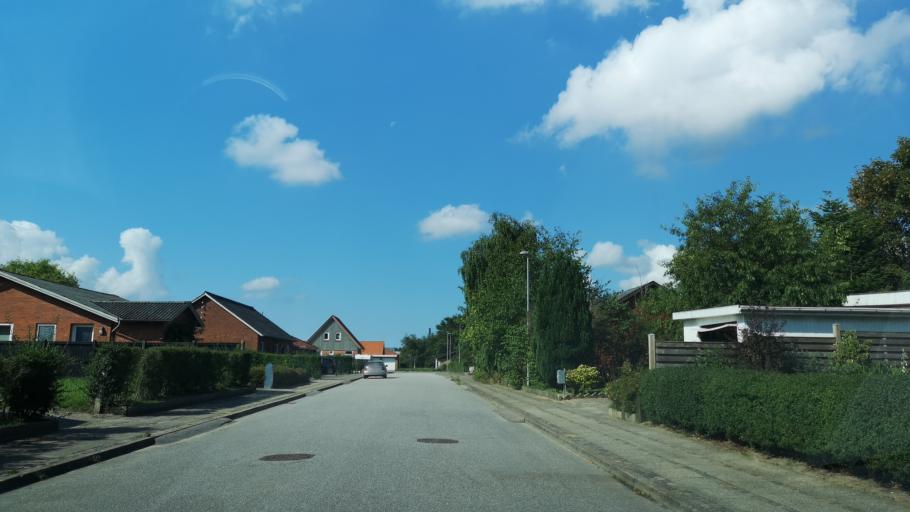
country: DK
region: Central Jutland
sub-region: Ringkobing-Skjern Kommune
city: Skjern
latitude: 55.9536
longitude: 8.4973
